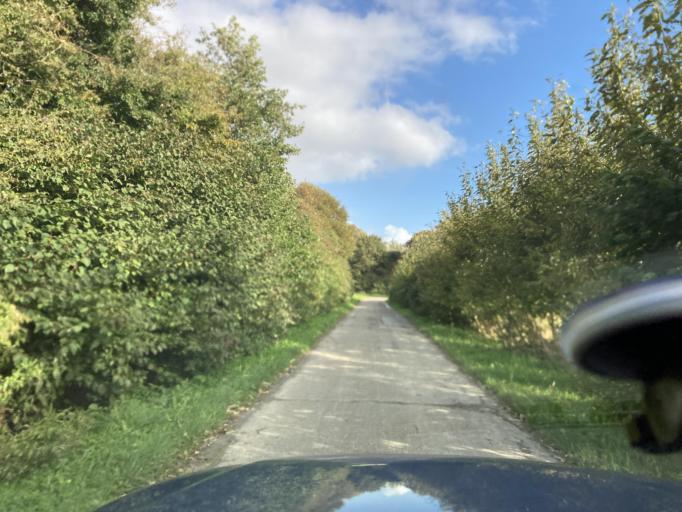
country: DE
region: Schleswig-Holstein
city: Oesterdeichstrich
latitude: 54.1528
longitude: 8.8955
